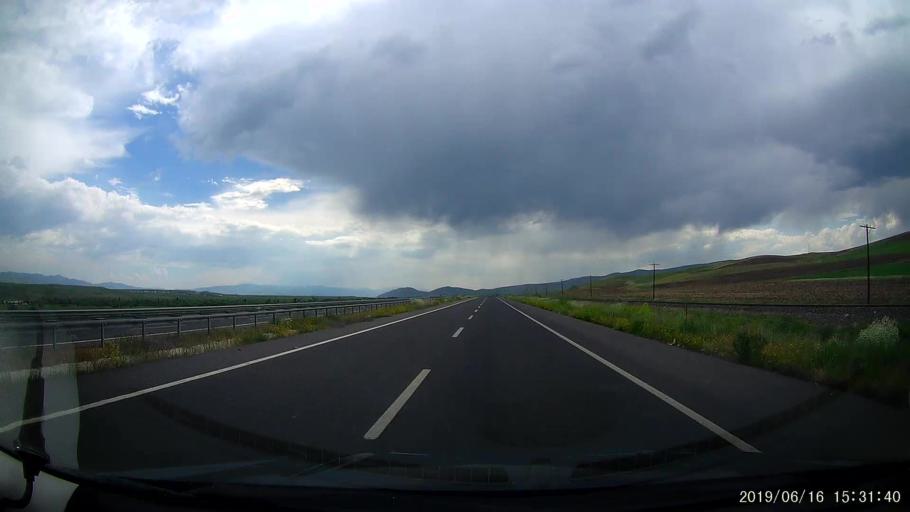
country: TR
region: Erzurum
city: Horasan
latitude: 40.0315
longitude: 42.0715
